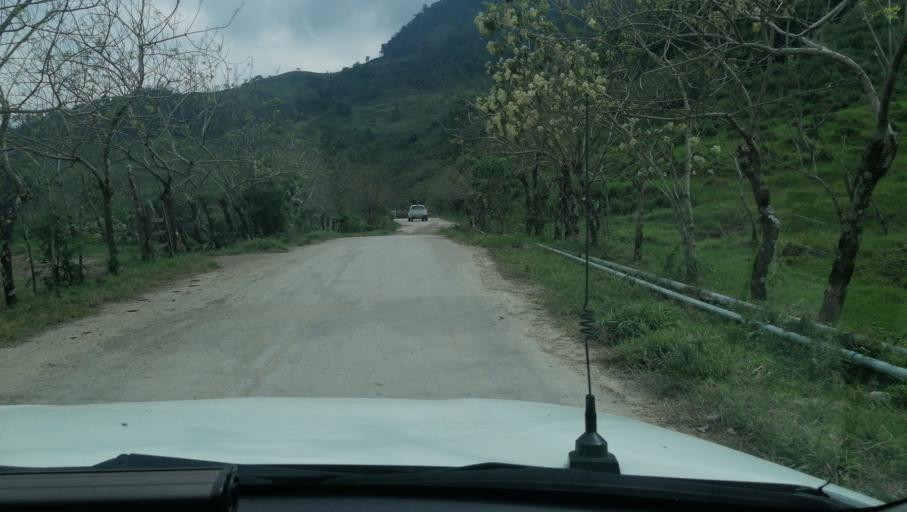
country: MX
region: Chiapas
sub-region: Francisco Leon
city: San Miguel la Sardina
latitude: 17.2813
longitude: -93.2752
